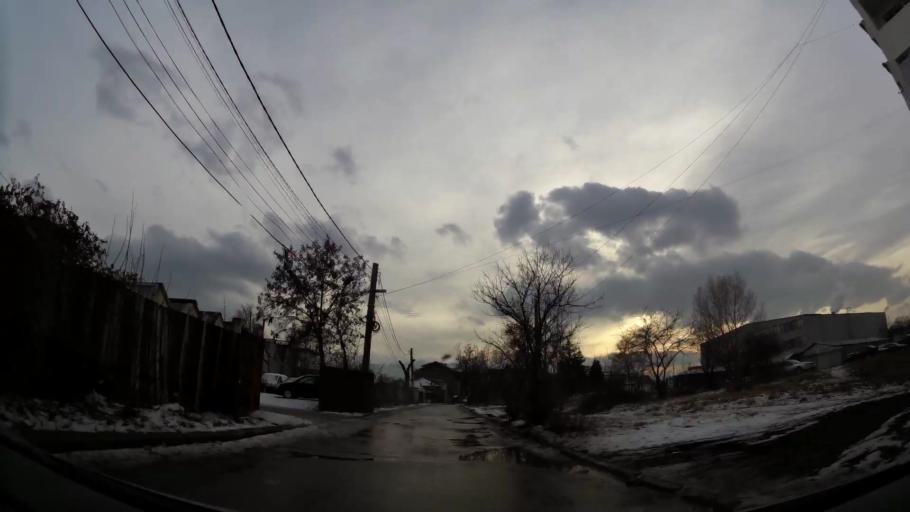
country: BG
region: Sofia-Capital
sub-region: Stolichna Obshtina
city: Sofia
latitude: 42.7228
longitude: 23.3367
